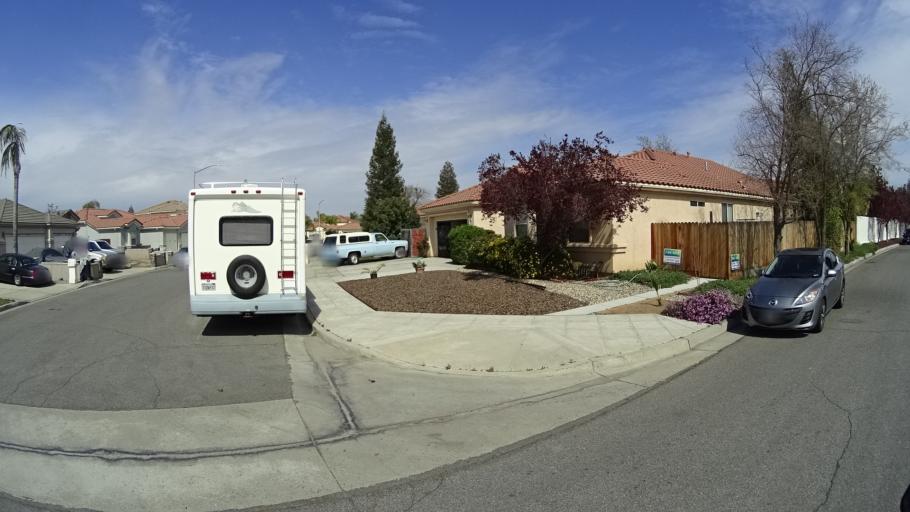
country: US
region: California
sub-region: Fresno County
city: Biola
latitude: 36.8487
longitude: -119.8990
